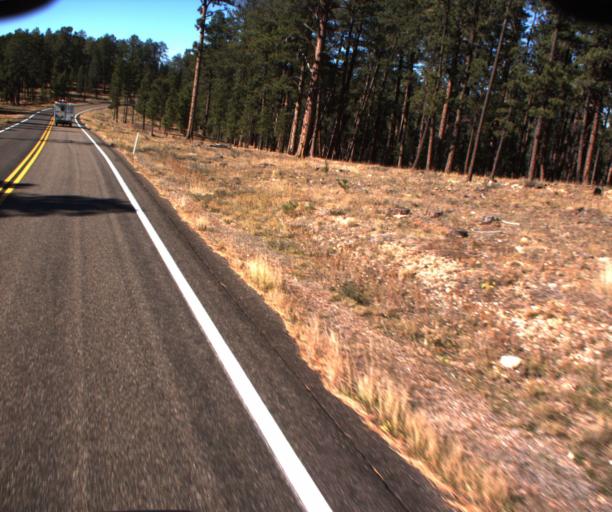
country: US
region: Arizona
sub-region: Coconino County
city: Fredonia
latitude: 36.6702
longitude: -112.2047
